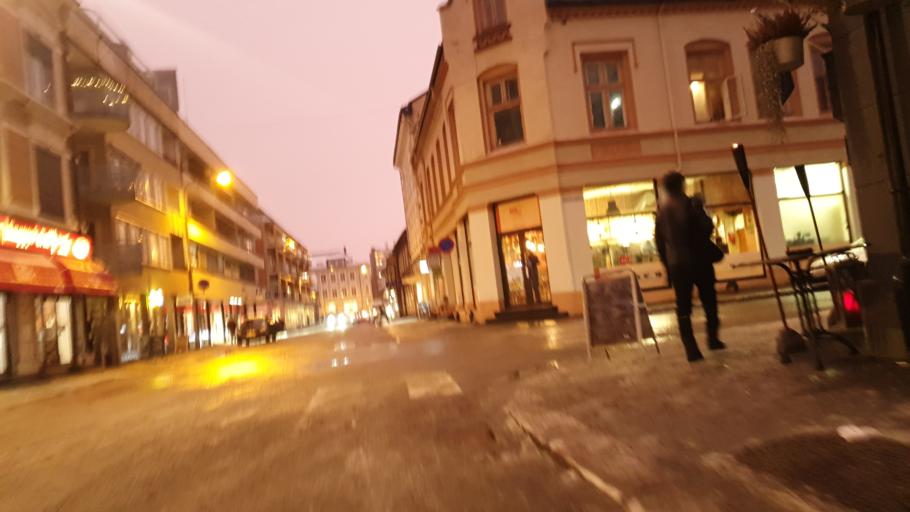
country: NO
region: Buskerud
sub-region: Drammen
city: Drammen
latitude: 59.7390
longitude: 10.2041
